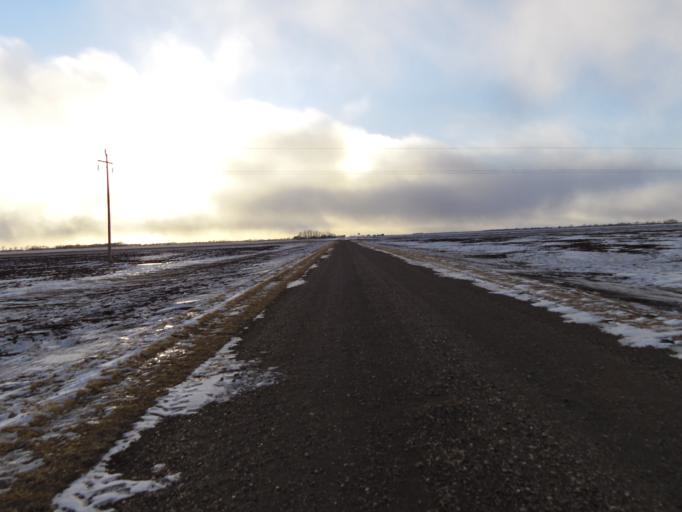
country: US
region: North Dakota
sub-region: Walsh County
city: Grafton
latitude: 48.3976
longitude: -97.2313
